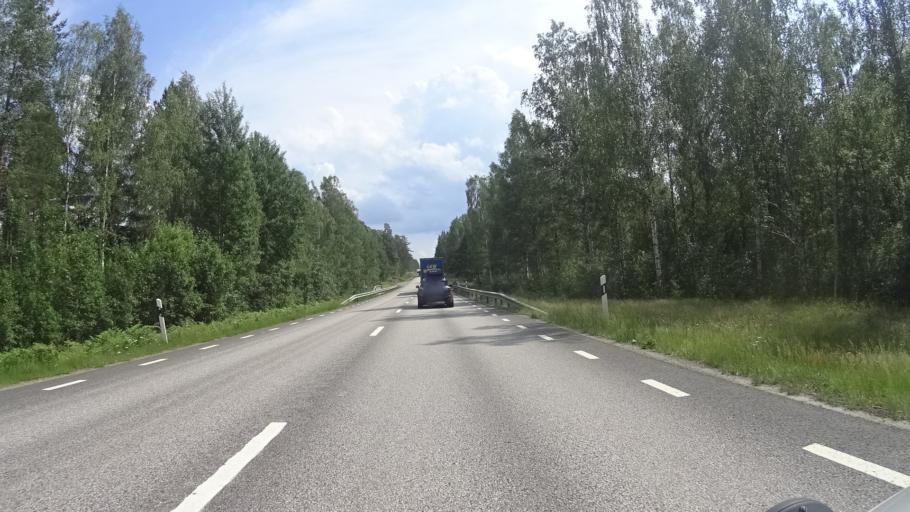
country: SE
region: Kalmar
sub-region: Hultsfreds Kommun
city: Hultsfred
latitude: 57.4835
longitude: 15.8311
